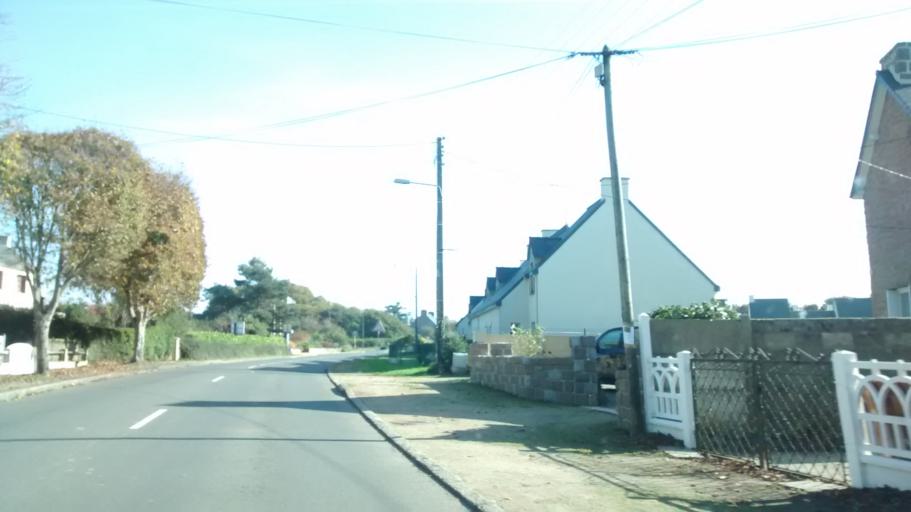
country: FR
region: Brittany
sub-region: Departement des Cotes-d'Armor
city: Trebeurden
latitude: 48.7674
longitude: -3.5535
